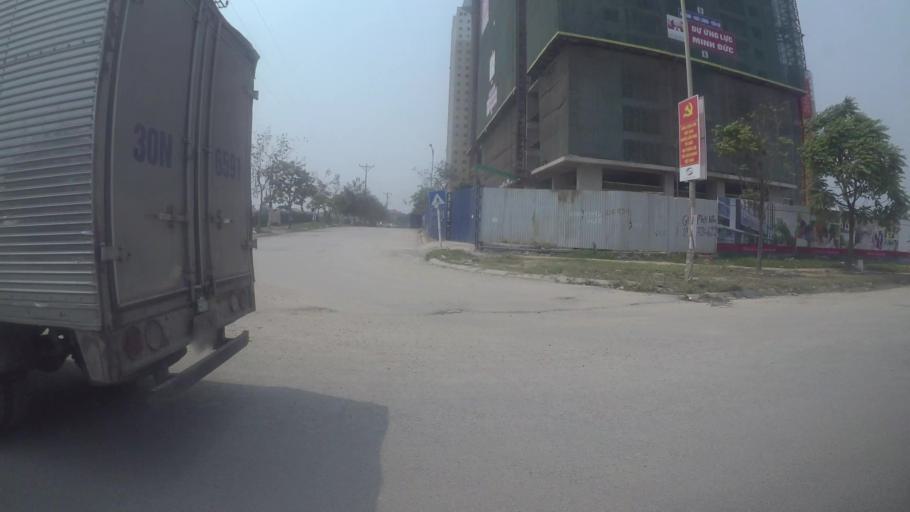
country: VN
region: Ha Noi
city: Cau Dien
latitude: 21.0105
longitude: 105.7227
